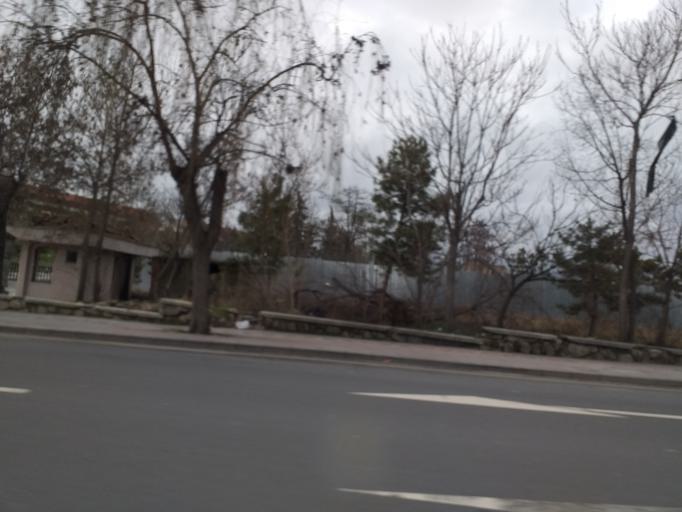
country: TR
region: Ankara
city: Ankara
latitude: 39.9684
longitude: 32.8369
